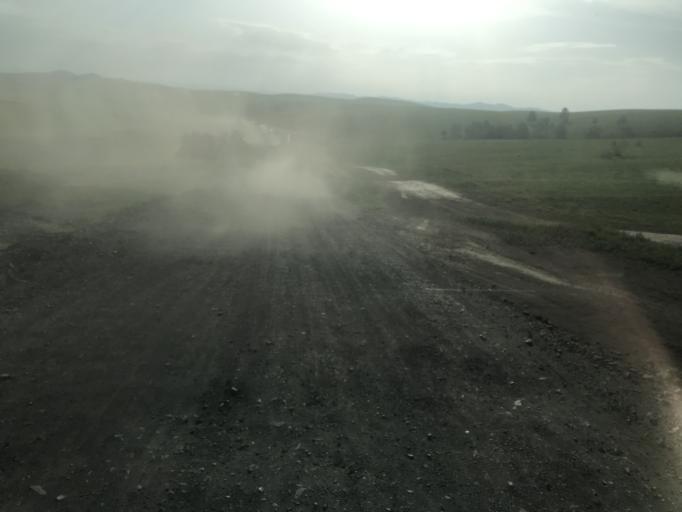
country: MN
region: Central Aimak
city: Javhlant
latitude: 48.6496
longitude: 106.0987
